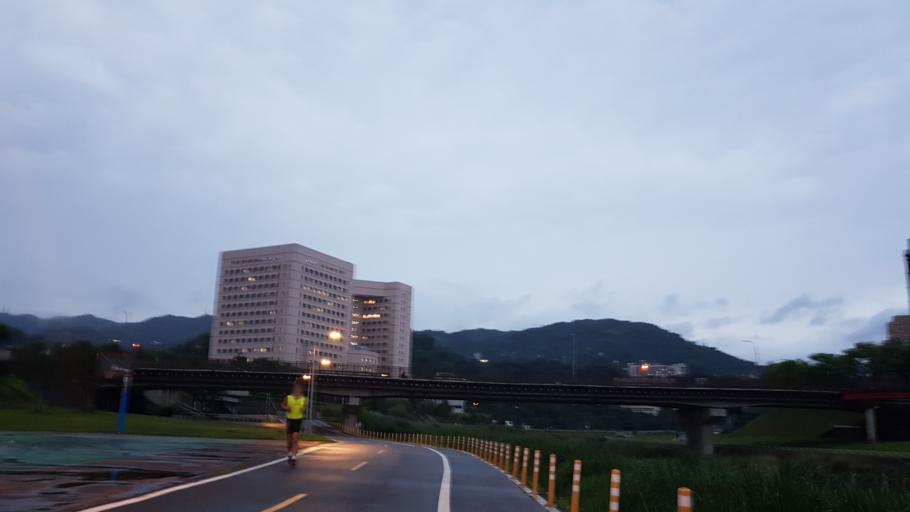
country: TW
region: Taipei
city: Taipei
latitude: 24.9889
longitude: 121.5721
